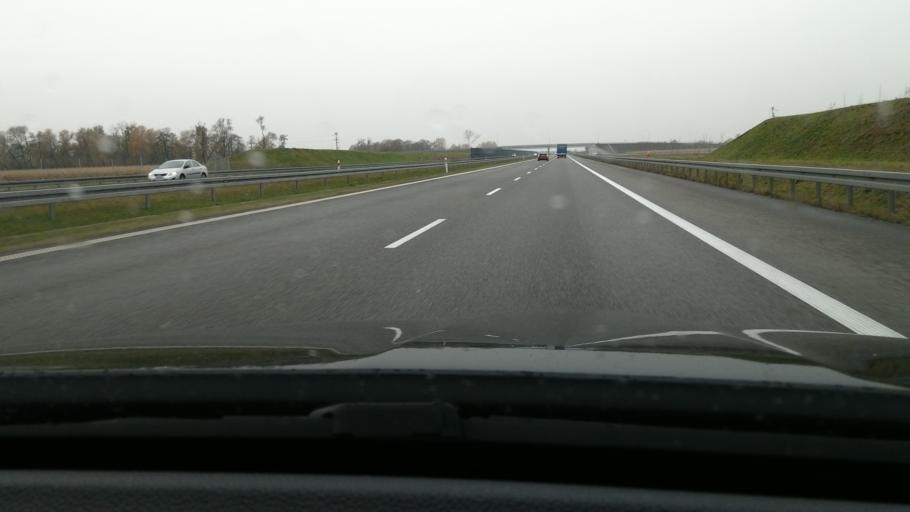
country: PL
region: Masovian Voivodeship
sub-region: Powiat warszawski zachodni
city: Bieniewice
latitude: 52.1344
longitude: 20.5606
